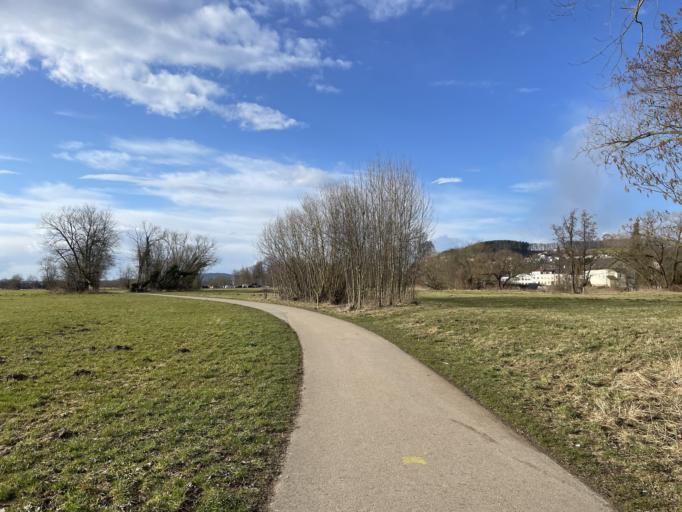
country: DE
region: Bavaria
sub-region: Upper Palatinate
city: Cham
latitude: 49.2159
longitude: 12.6624
